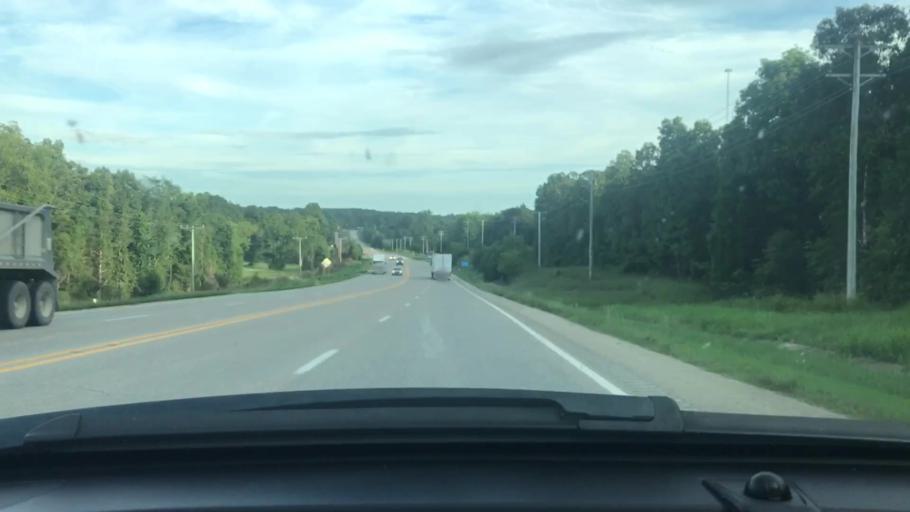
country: US
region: Arkansas
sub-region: Lawrence County
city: Hoxie
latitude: 36.1264
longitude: -91.1554
